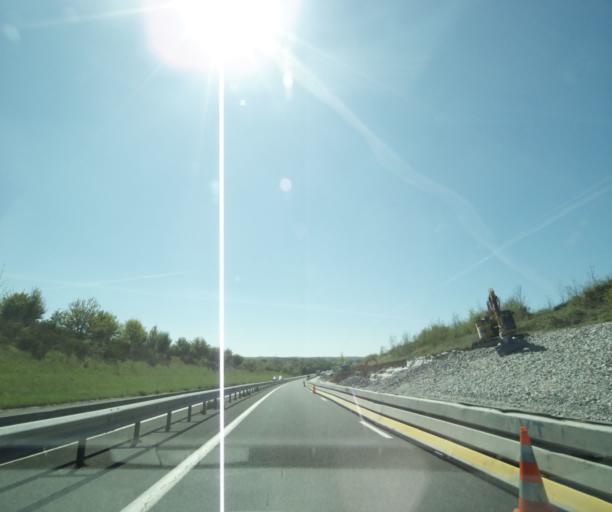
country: FR
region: Centre
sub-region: Departement de l'Indre
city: Le Pechereau
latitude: 46.5302
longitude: 1.5146
